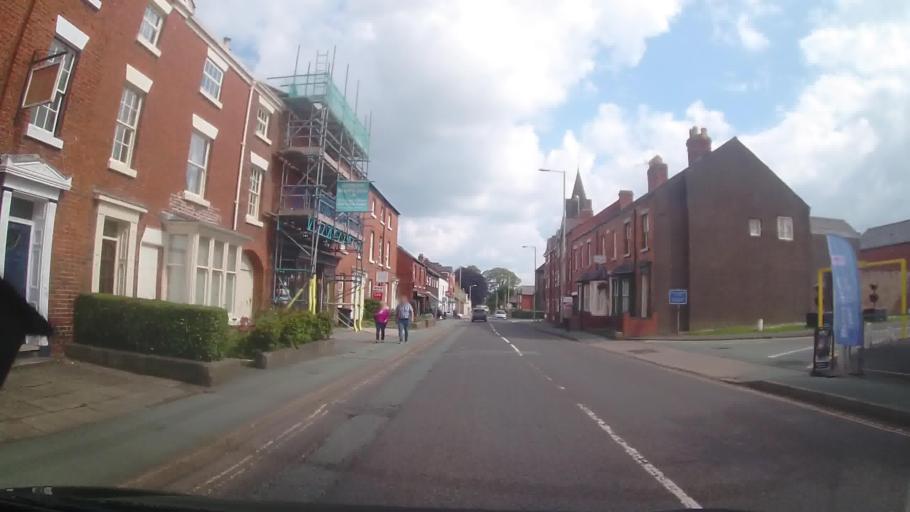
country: GB
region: England
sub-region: Shropshire
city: Oswestry
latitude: 52.8584
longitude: -3.0524
